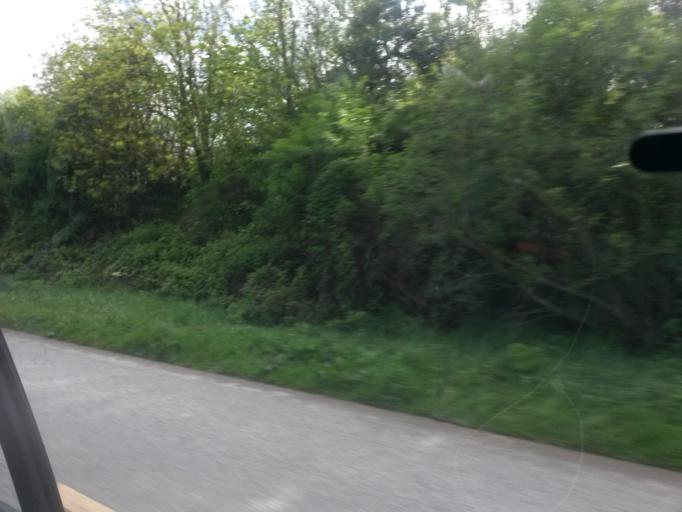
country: IE
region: Leinster
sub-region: Loch Garman
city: Enniscorthy
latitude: 52.5377
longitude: -6.5530
